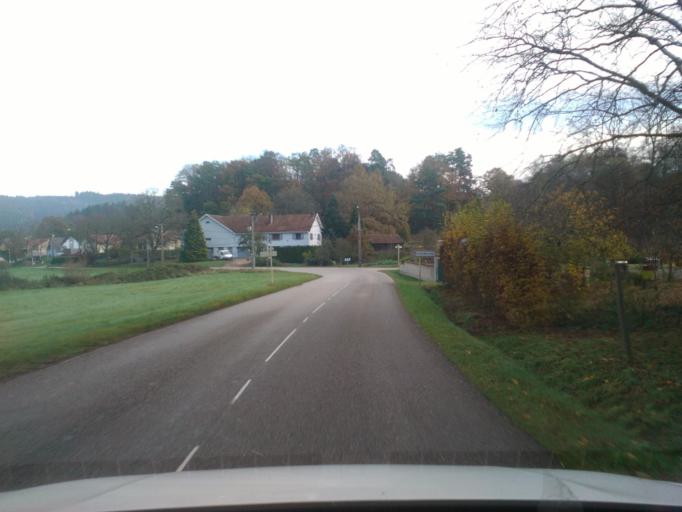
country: FR
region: Lorraine
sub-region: Departement des Vosges
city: Moyenmoutier
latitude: 48.3453
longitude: 6.9307
